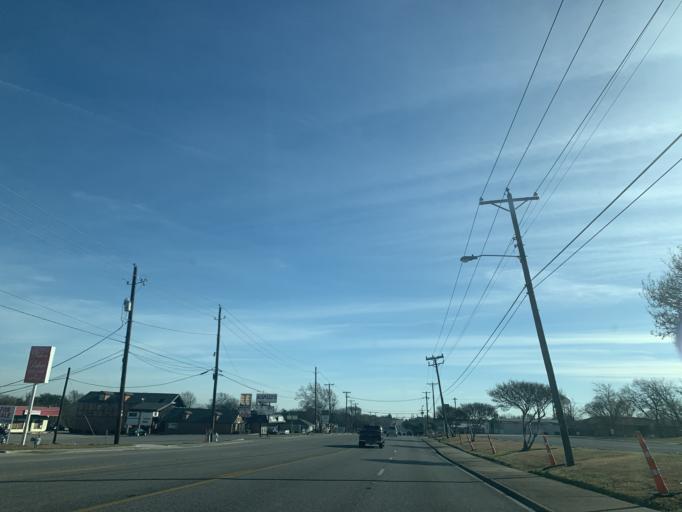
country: US
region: Texas
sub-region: Dallas County
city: DeSoto
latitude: 32.5896
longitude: -96.8548
